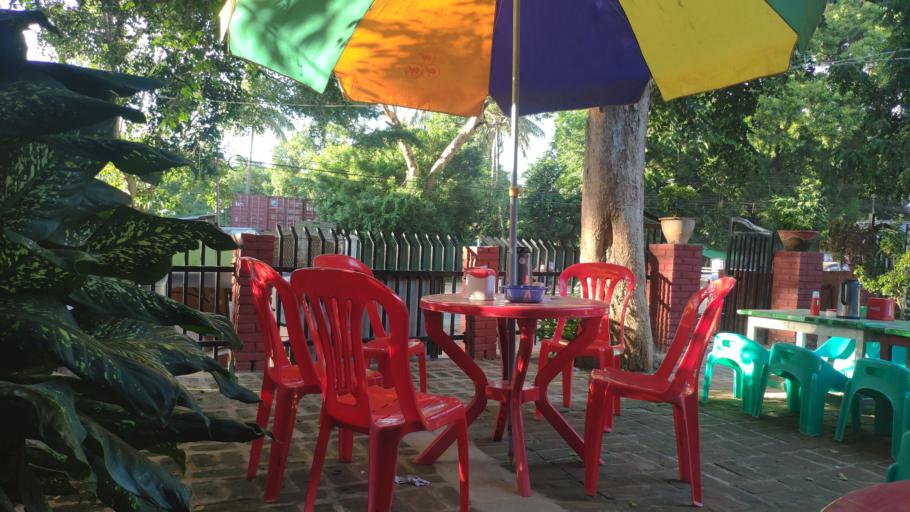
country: MM
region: Magway
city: Pakokku
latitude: 21.1874
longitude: 94.8901
